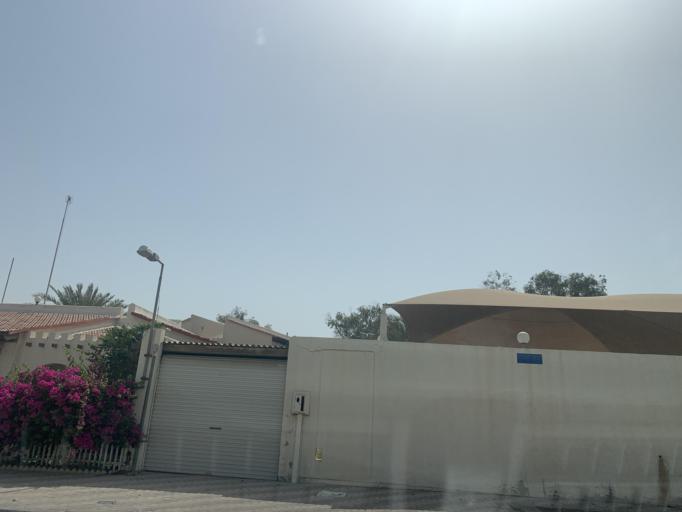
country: BH
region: Northern
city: Madinat `Isa
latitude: 26.1514
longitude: 50.5307
